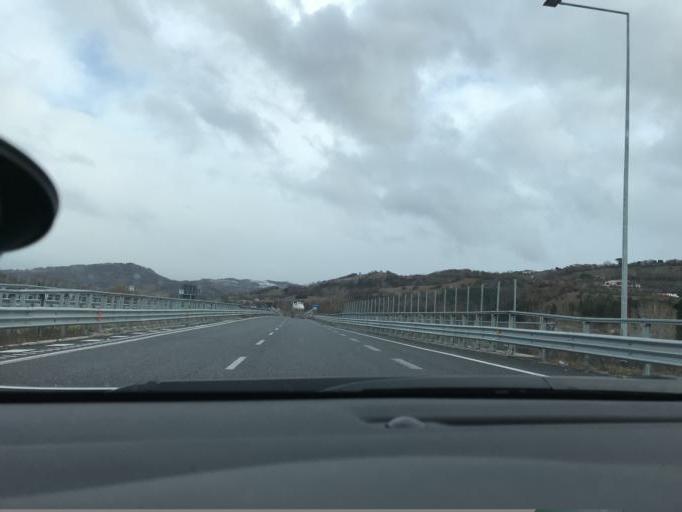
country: IT
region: Umbria
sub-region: Provincia di Perugia
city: Valfabbrica
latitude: 43.1596
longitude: 12.5939
